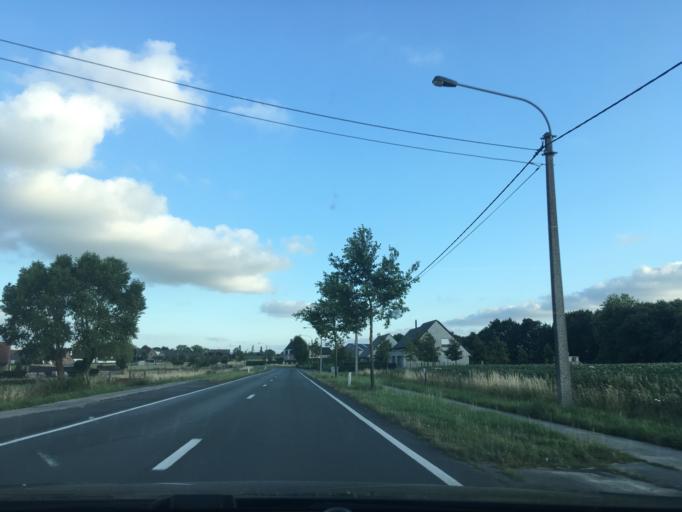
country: BE
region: Flanders
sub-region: Provincie West-Vlaanderen
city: Tielt
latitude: 51.0187
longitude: 3.3095
